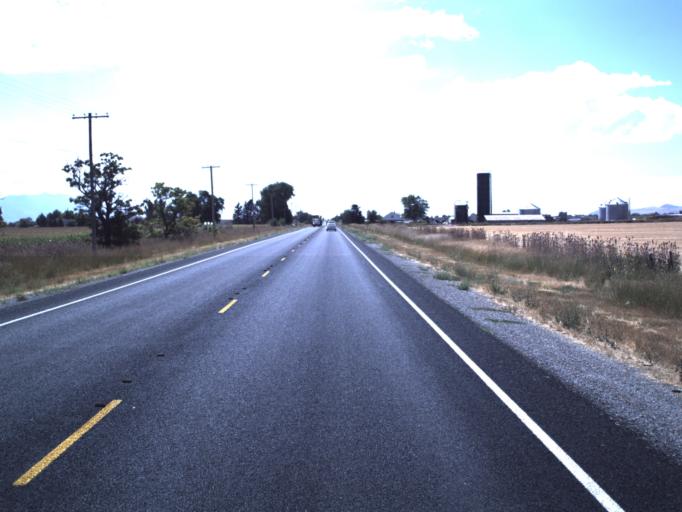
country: US
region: Utah
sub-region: Box Elder County
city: Garland
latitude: 41.7742
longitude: -112.1491
